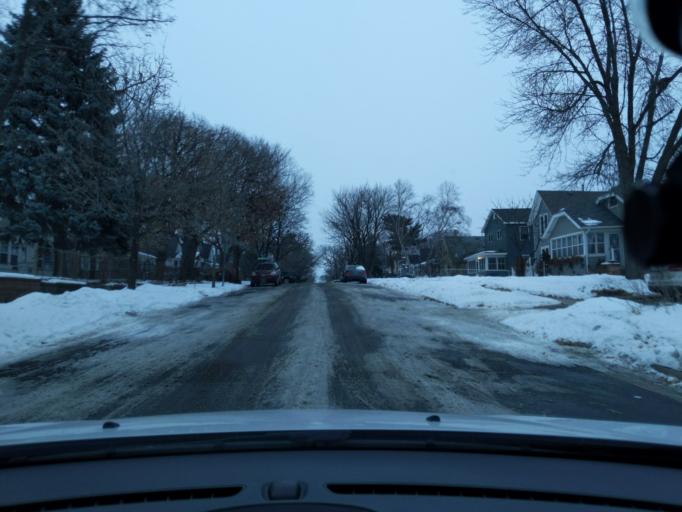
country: US
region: Minnesota
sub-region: Ramsey County
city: Falcon Heights
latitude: 44.9648
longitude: -93.1798
